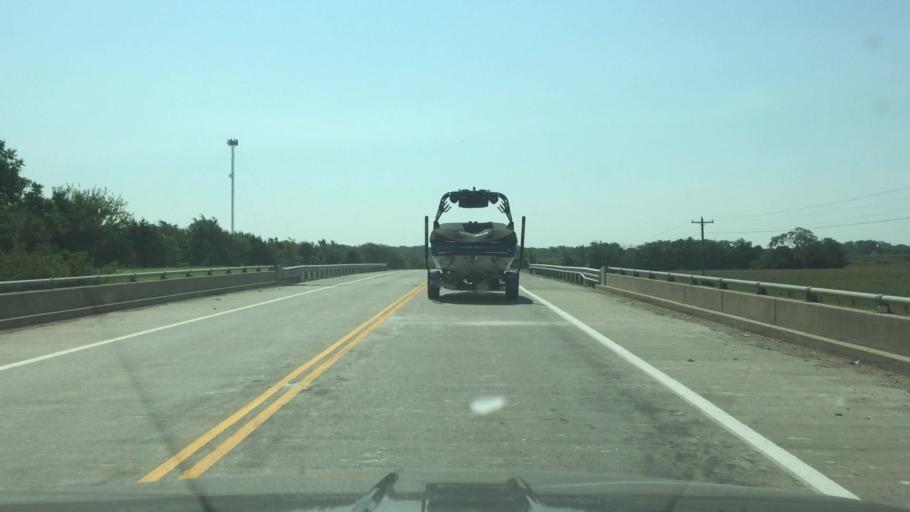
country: US
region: Missouri
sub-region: Pettis County
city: Sedalia
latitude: 38.6854
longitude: -93.0378
